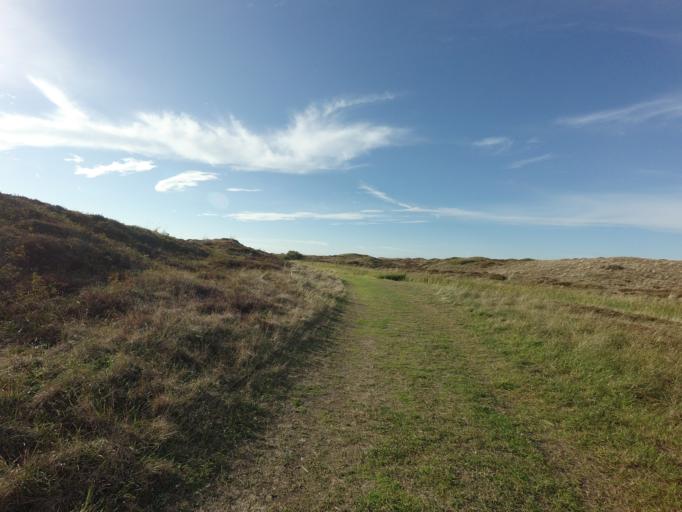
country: NL
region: North Holland
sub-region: Gemeente Den Helder
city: Den Helder
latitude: 53.0117
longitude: 4.7428
